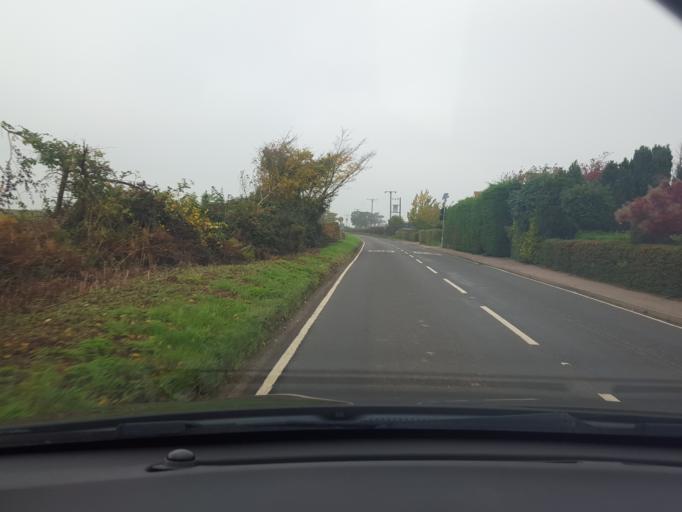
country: GB
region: England
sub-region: Essex
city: Alresford
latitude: 51.8963
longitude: 1.0241
